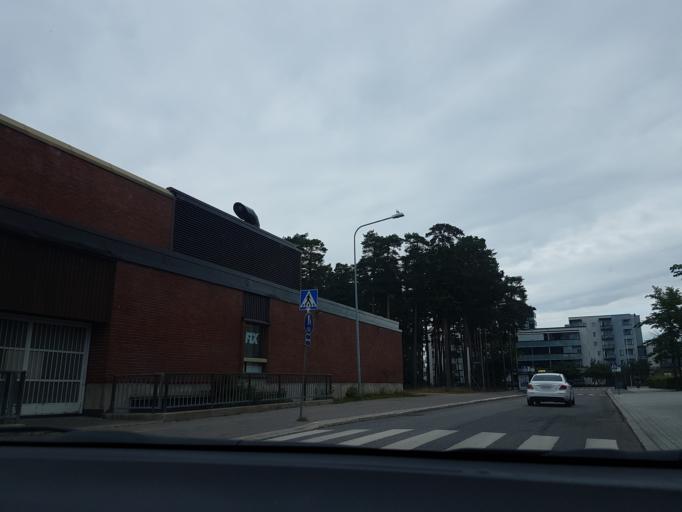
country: FI
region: Uusimaa
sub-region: Helsinki
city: Vantaa
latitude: 60.2086
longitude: 25.1428
